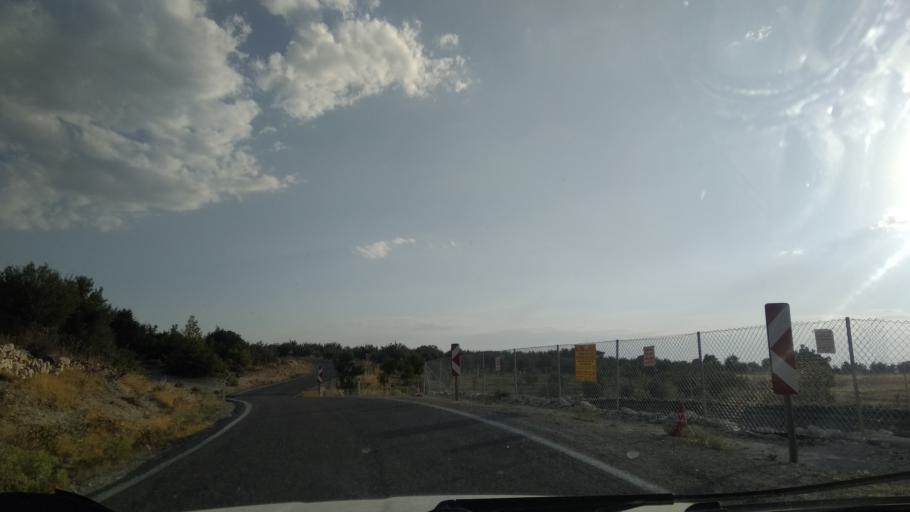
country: TR
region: Mersin
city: Sarikavak
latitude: 36.5699
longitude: 33.6347
